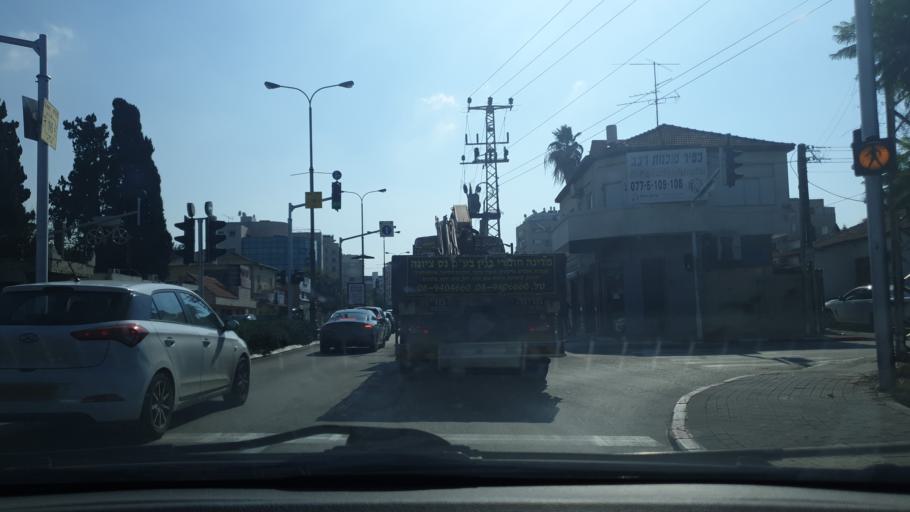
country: IL
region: Central District
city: Rishon LeZiyyon
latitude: 31.9733
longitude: 34.8067
